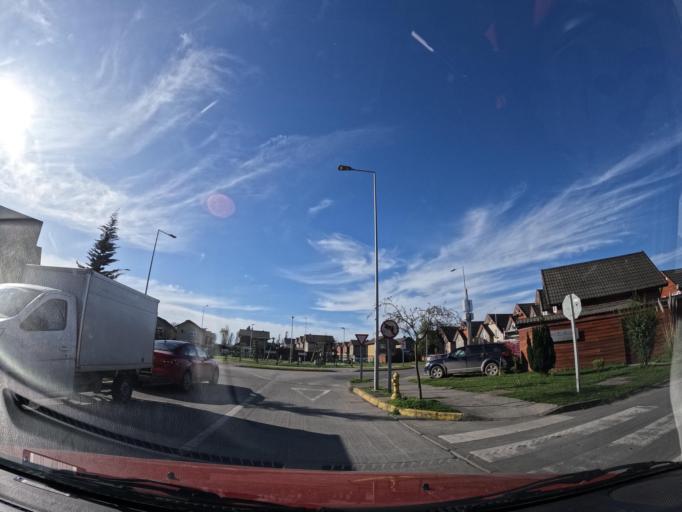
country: CL
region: Biobio
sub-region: Provincia de Concepcion
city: Concepcion
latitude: -36.7695
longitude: -73.0679
